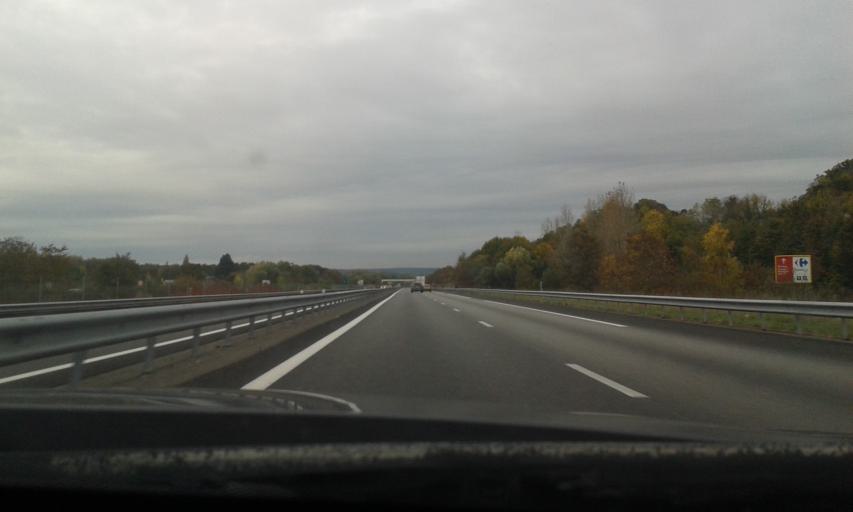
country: FR
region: Haute-Normandie
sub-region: Departement de l'Eure
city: Louviers
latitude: 49.2133
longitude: 1.1811
